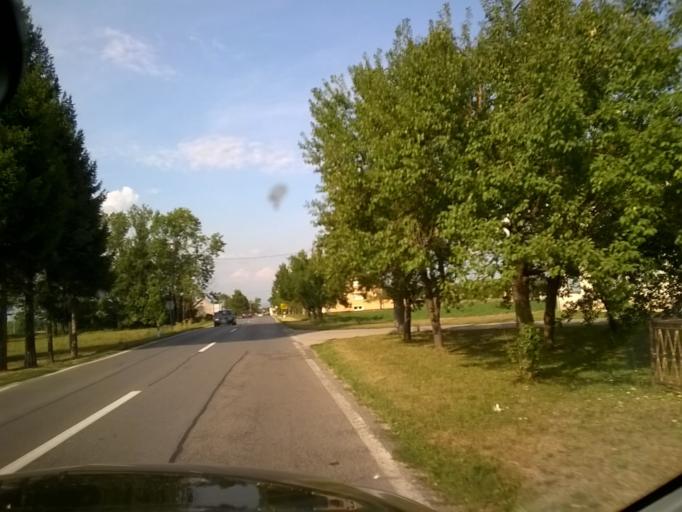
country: HR
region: Licko-Senjska
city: Gospic
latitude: 44.5329
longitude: 15.3428
